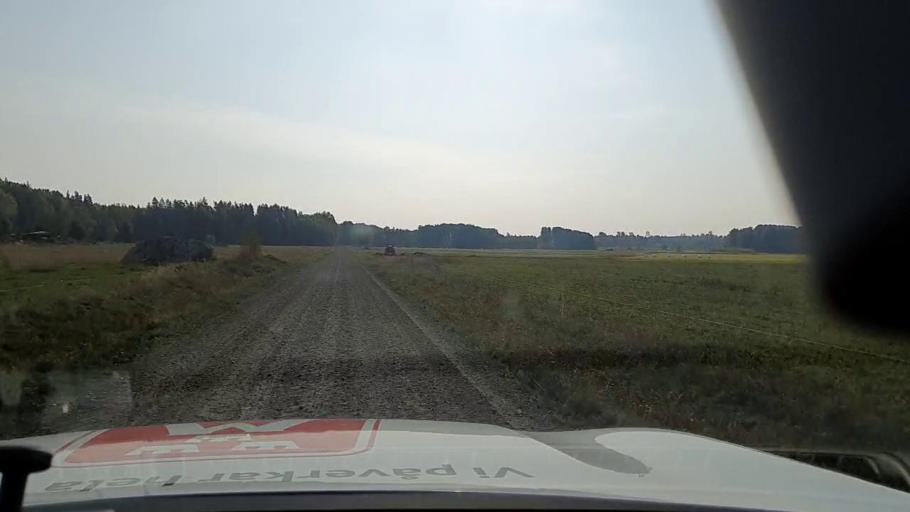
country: SE
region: Vaestmanland
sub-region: Kungsors Kommun
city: Kungsoer
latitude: 59.3541
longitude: 16.1597
